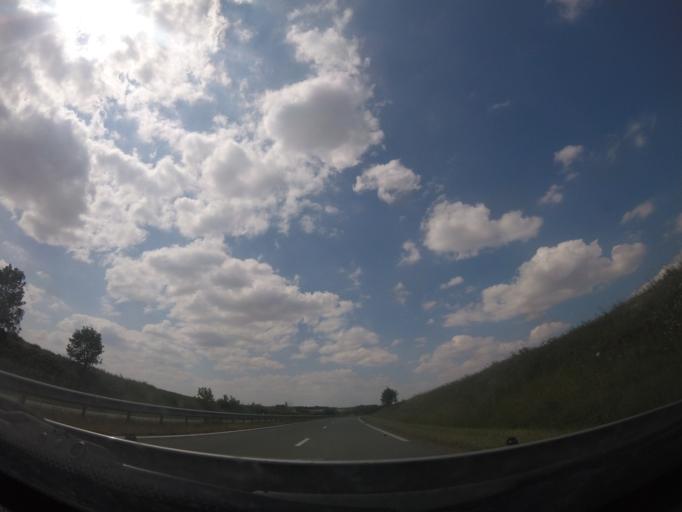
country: FR
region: Poitou-Charentes
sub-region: Departement de la Charente-Maritime
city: Saint-Porchaire
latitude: 45.8152
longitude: -0.7861
